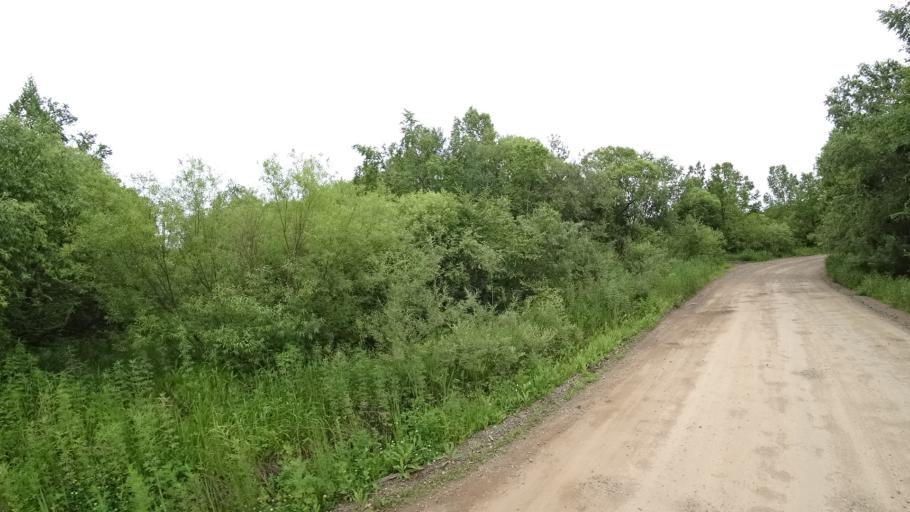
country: RU
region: Primorskiy
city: Arsen'yev
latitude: 44.1917
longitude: 133.3106
